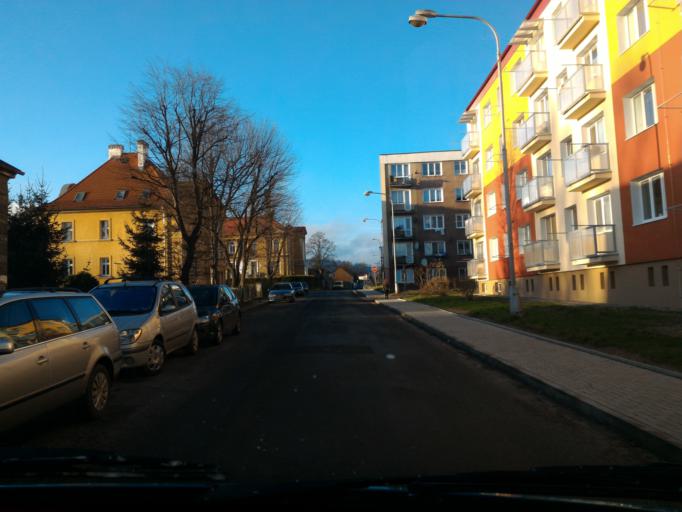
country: CZ
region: Ustecky
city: Varnsdorf
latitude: 50.9127
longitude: 14.6298
